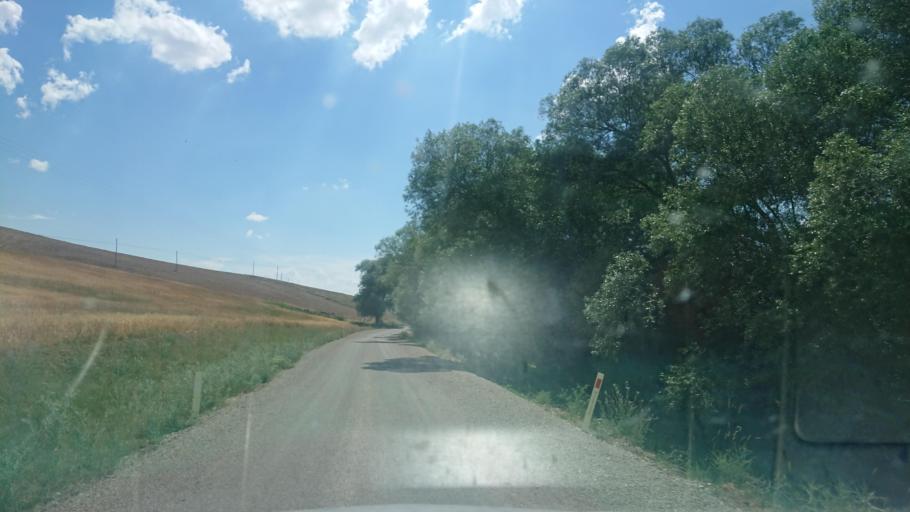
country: TR
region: Aksaray
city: Agacoren
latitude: 38.8358
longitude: 33.8037
